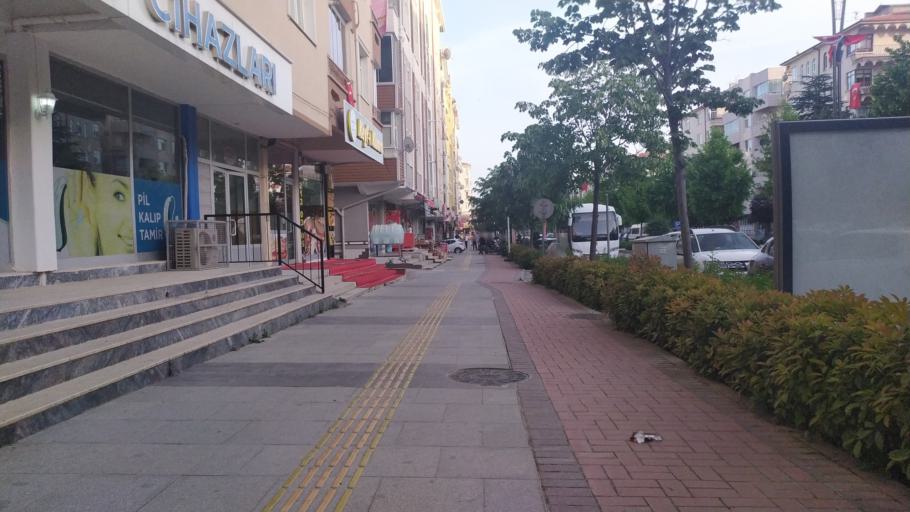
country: TR
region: Kirsehir
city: Kirsehir
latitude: 39.1534
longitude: 34.1596
